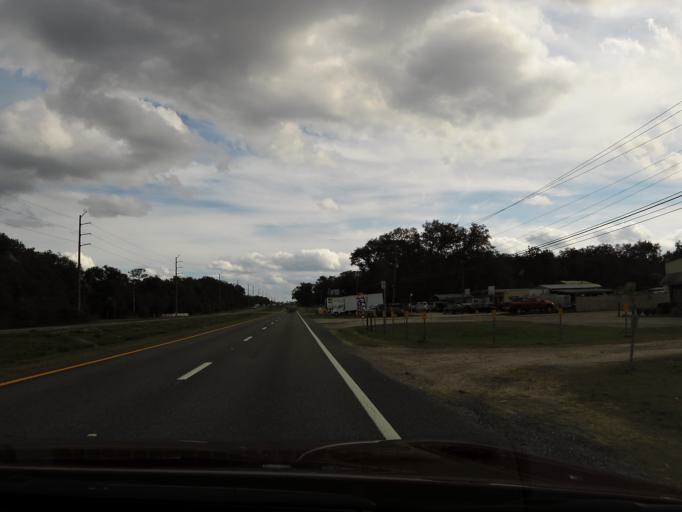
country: US
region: Florida
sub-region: Volusia County
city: De Leon Springs
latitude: 29.0976
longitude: -81.3352
